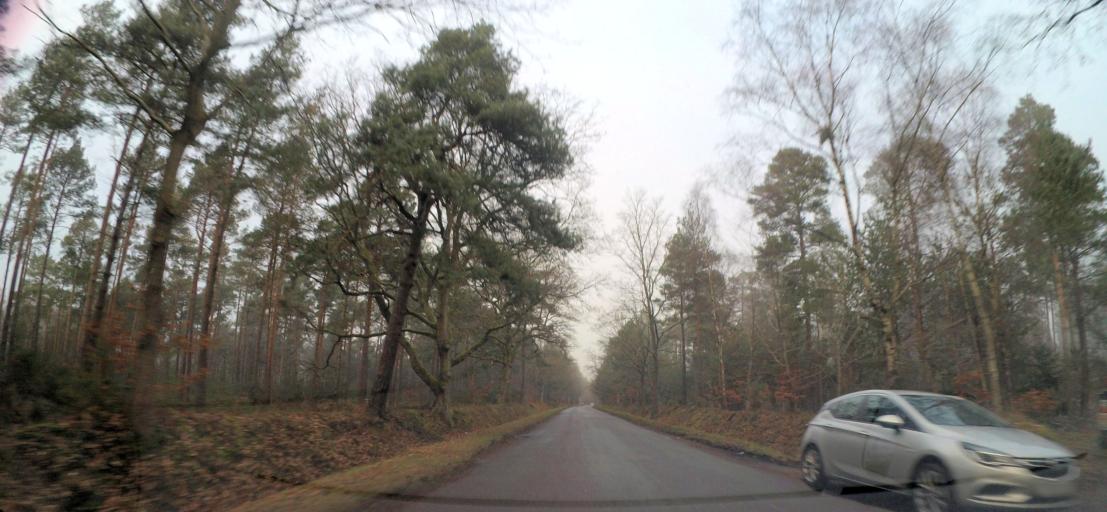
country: GB
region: England
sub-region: West Berkshire
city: Theale
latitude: 51.3863
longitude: -1.0884
